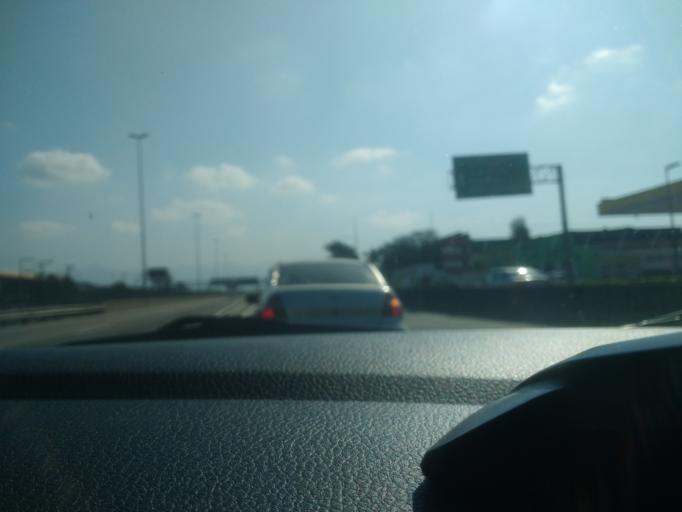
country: BR
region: Rio de Janeiro
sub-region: Duque De Caxias
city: Duque de Caxias
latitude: -22.6796
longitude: -43.2855
